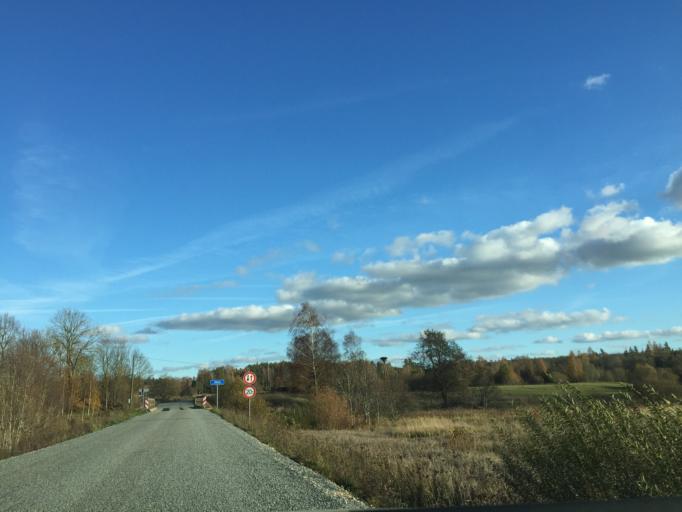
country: LV
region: Tukuma Rajons
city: Tukums
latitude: 56.9369
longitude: 22.9578
